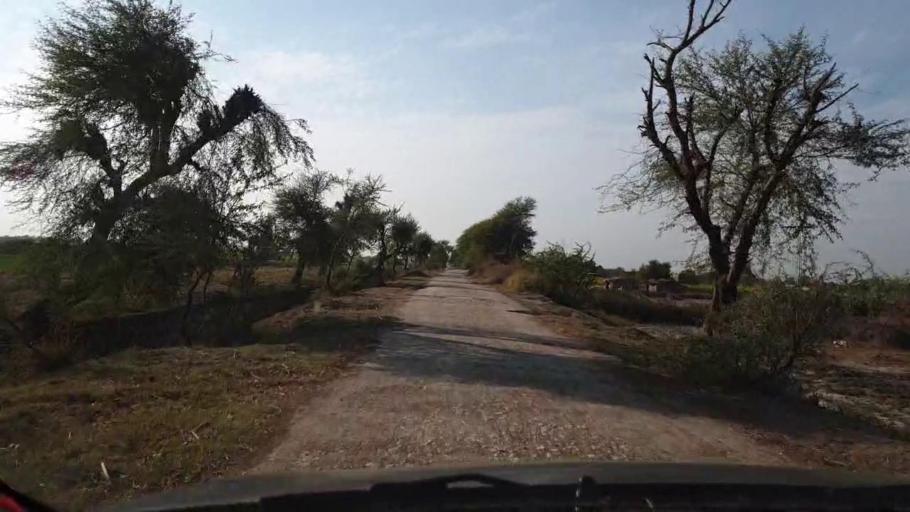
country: PK
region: Sindh
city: Sinjhoro
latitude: 25.9771
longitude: 68.8195
